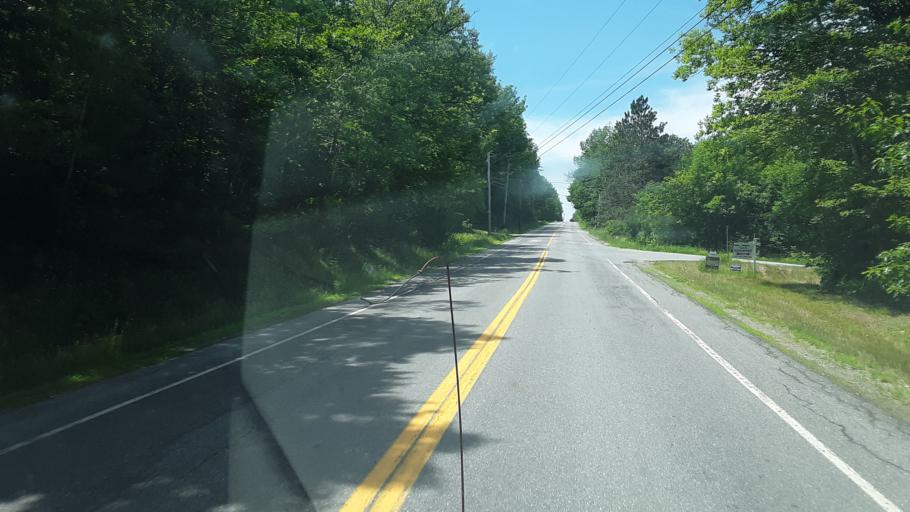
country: US
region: Maine
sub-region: Hancock County
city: Bucksport
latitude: 44.5705
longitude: -68.8233
